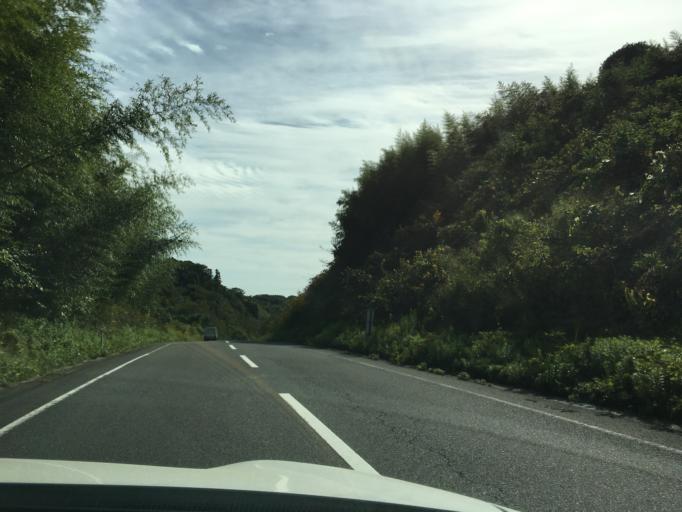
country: JP
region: Fukushima
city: Nihommatsu
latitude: 37.5537
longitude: 140.4995
